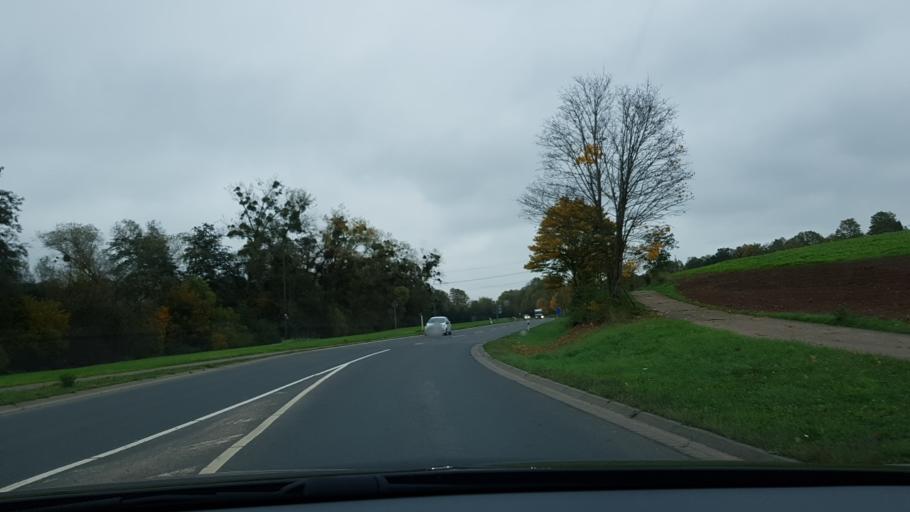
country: DE
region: Rheinland-Pfalz
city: Schweich
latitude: 49.8321
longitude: 6.7586
